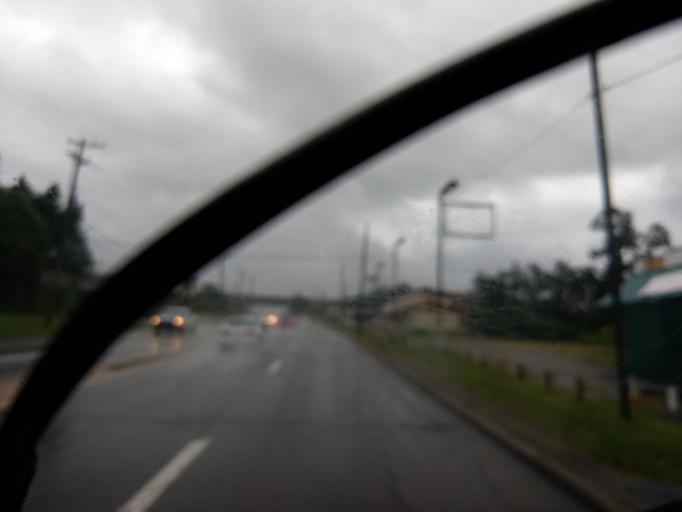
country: US
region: Pennsylvania
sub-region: Allegheny County
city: North Versailles
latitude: 40.3825
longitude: -79.8205
